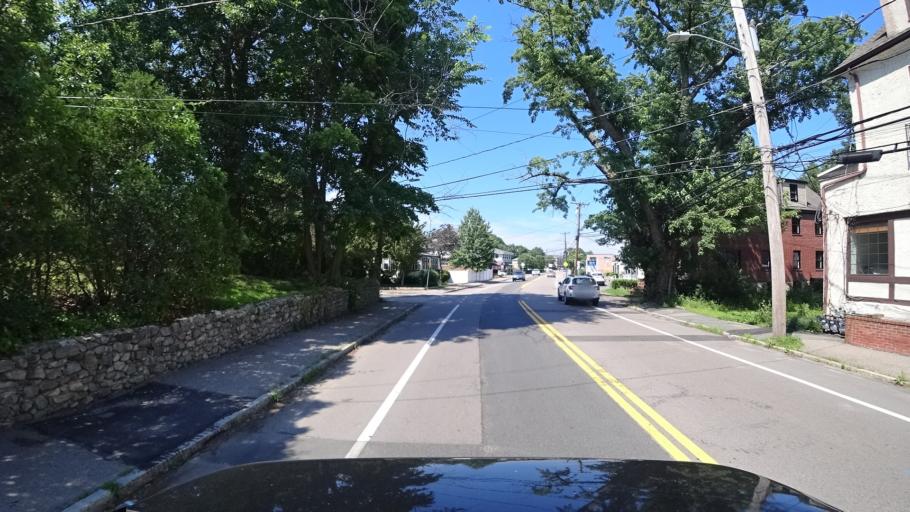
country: US
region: Massachusetts
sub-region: Norfolk County
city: Dedham
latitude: 42.2672
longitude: -71.1764
